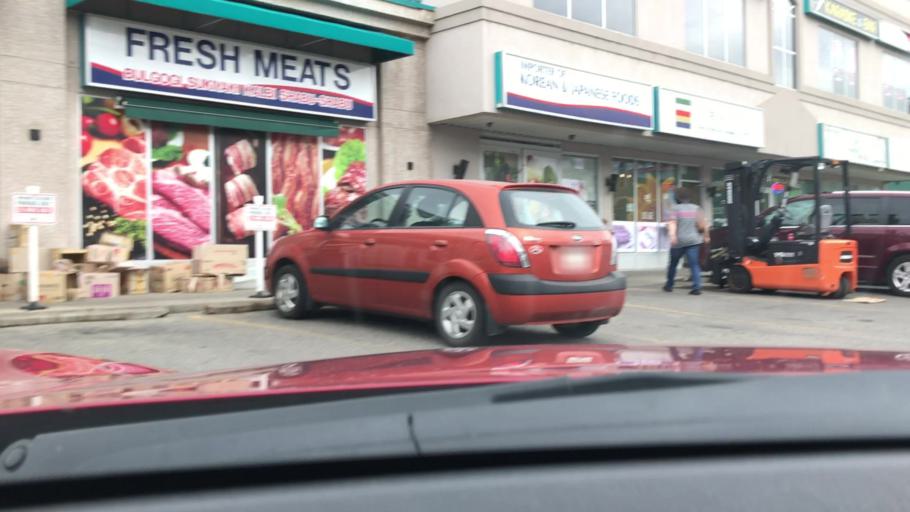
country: CA
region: Alberta
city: Calgary
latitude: 51.0445
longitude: -114.0926
